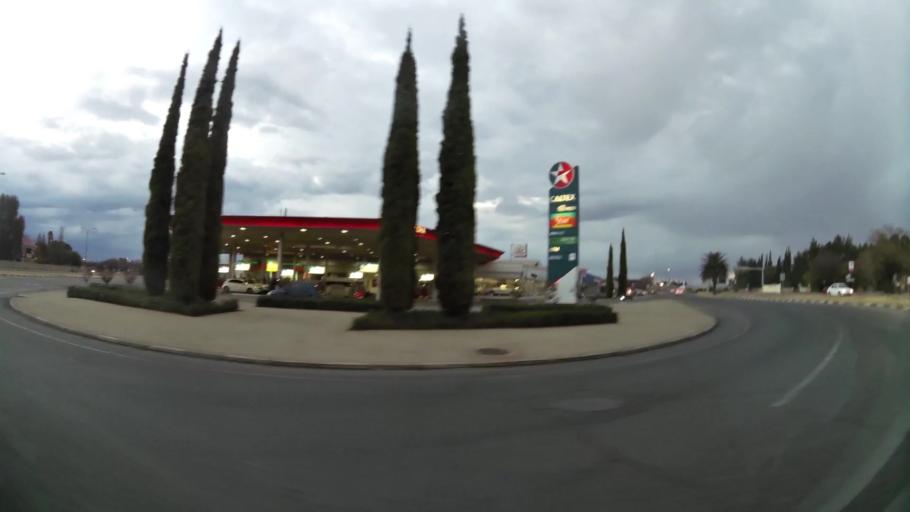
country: ZA
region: Orange Free State
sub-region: Lejweleputswa District Municipality
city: Welkom
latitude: -27.9810
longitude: 26.7608
